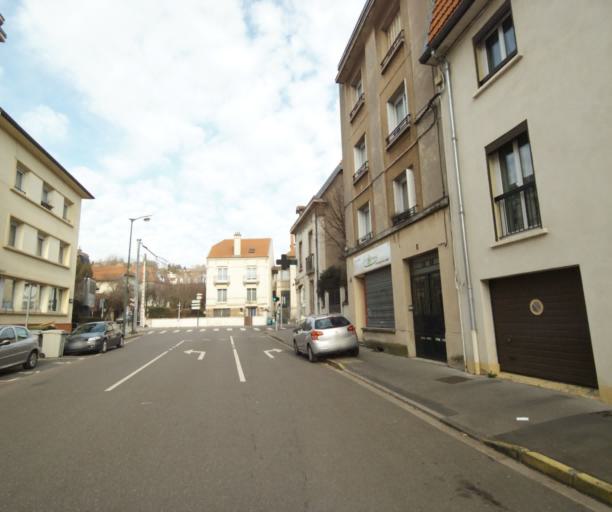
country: FR
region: Lorraine
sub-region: Departement de Meurthe-et-Moselle
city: Laxou
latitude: 48.6843
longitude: 6.1543
